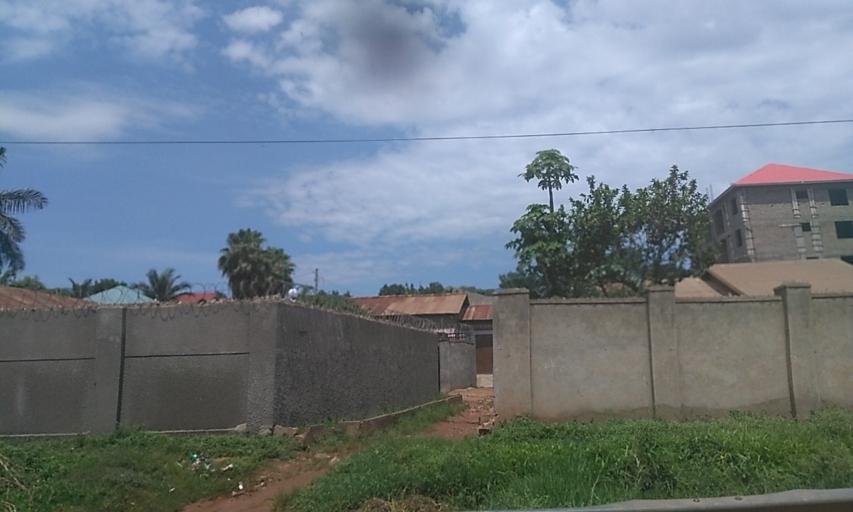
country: UG
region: Central Region
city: Kampala Central Division
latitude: 0.3512
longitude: 32.5784
